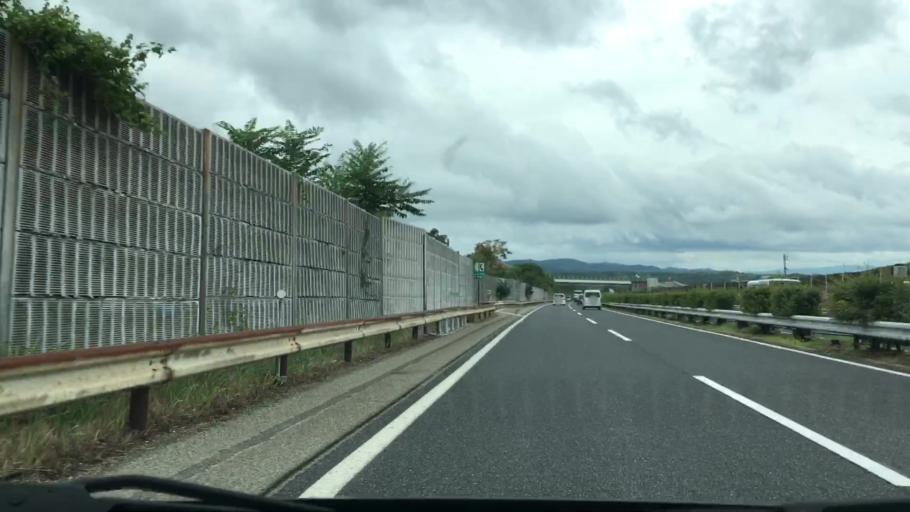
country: JP
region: Okayama
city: Tsuyama
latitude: 35.0225
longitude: 134.1832
